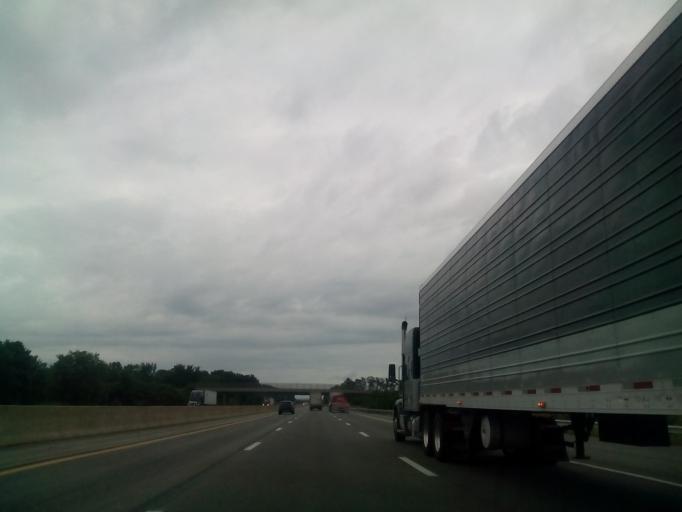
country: US
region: Ohio
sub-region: Huron County
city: Wakeman
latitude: 41.3329
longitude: -82.4198
